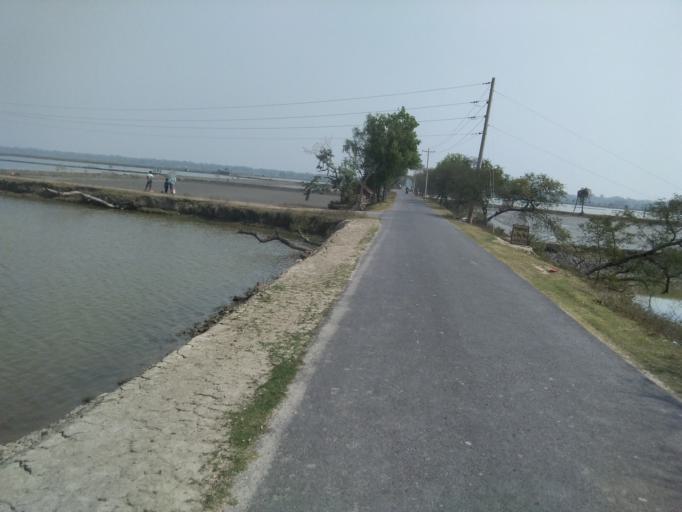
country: IN
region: West Bengal
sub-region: North 24 Parganas
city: Taki
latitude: 22.5939
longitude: 88.9808
